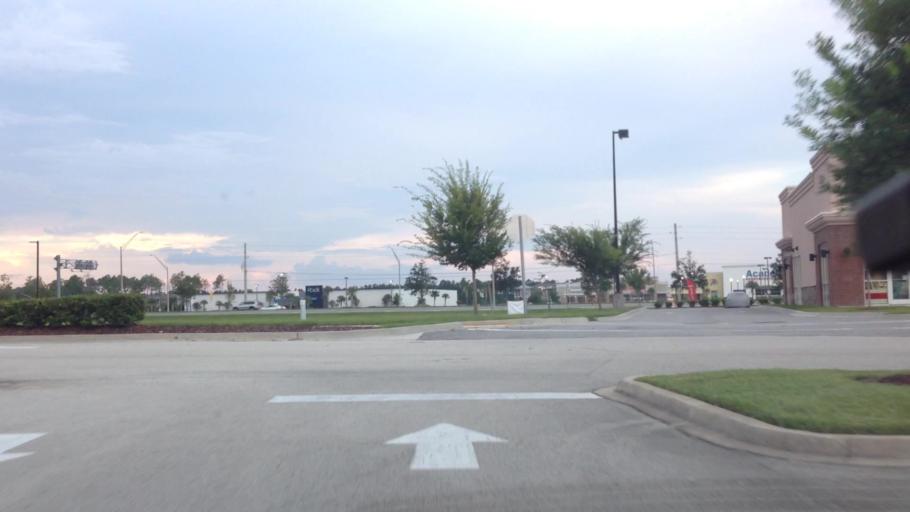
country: US
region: Florida
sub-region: Duval County
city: Atlantic Beach
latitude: 30.3196
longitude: -81.4950
